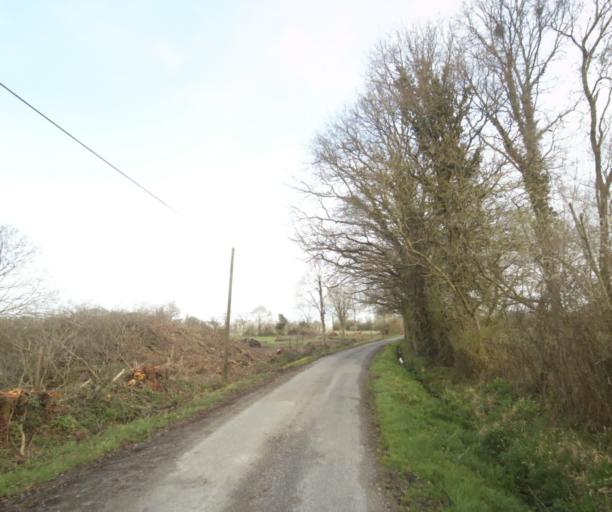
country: FR
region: Pays de la Loire
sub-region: Departement de la Loire-Atlantique
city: Bouvron
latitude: 47.4162
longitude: -1.8749
